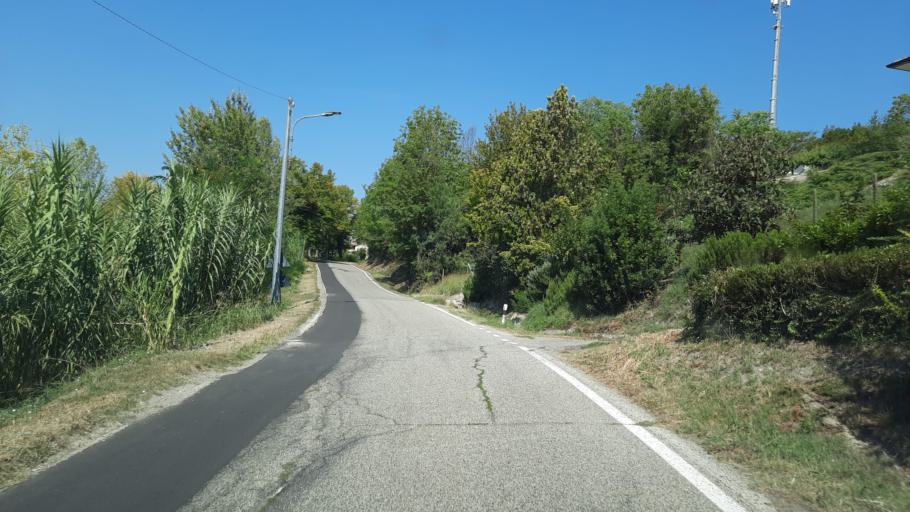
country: IT
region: Piedmont
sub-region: Provincia di Alessandria
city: Gabiano
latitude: 45.1560
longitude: 8.2044
